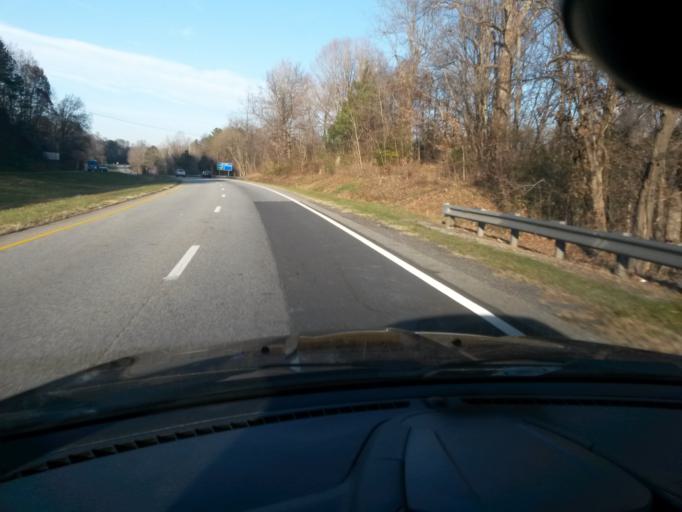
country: US
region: Virginia
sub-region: Amherst County
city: Amherst
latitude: 37.5692
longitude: -79.0536
